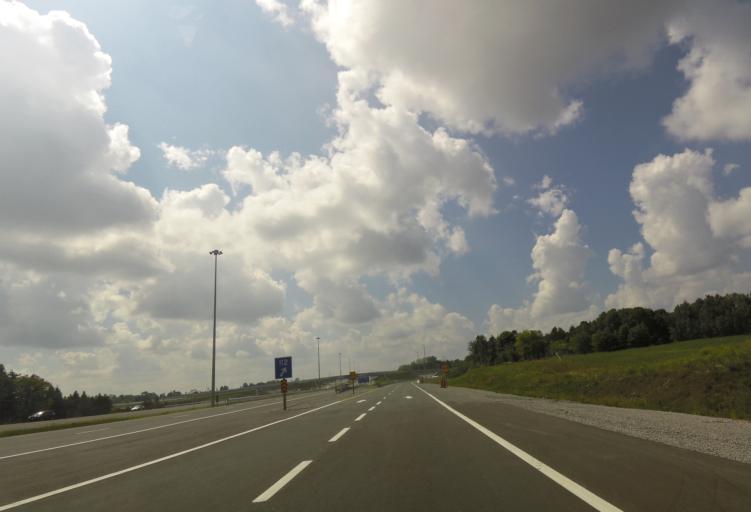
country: CA
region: Ontario
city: Ajax
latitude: 43.9516
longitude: -78.9968
